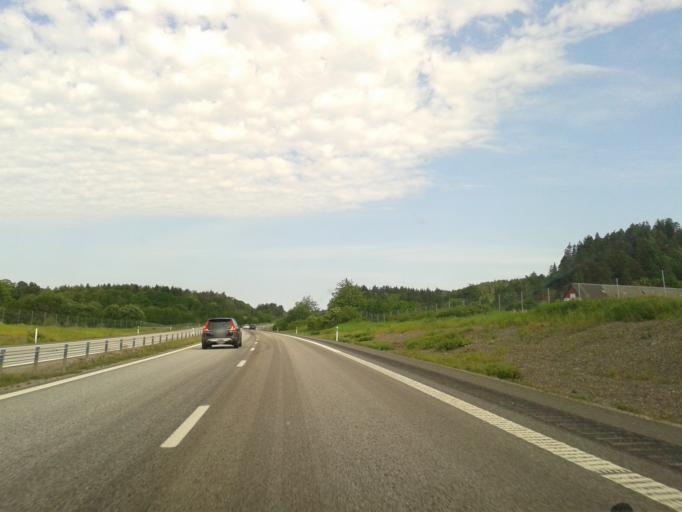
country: SE
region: Vaestra Goetaland
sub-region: Munkedals Kommun
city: Munkedal
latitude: 58.5423
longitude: 11.5229
